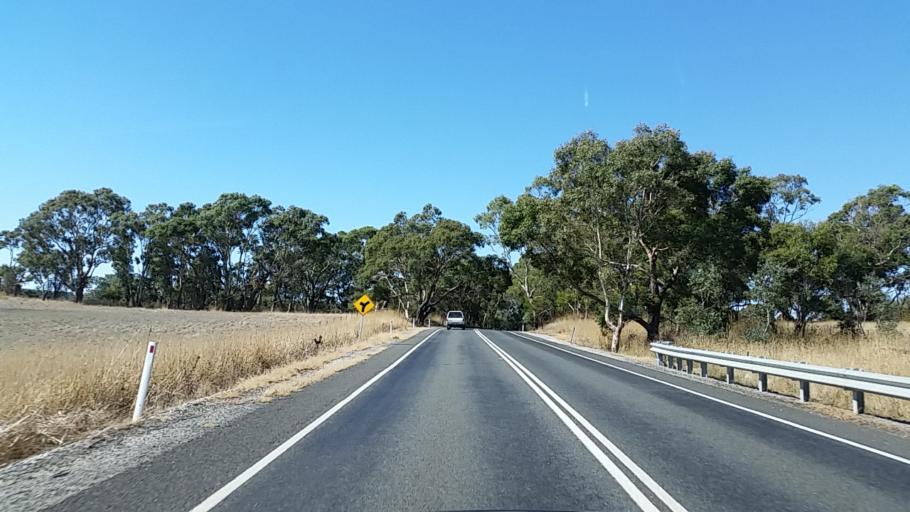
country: AU
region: South Australia
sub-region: Adelaide Hills
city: Birdwood
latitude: -34.7619
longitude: 139.0105
